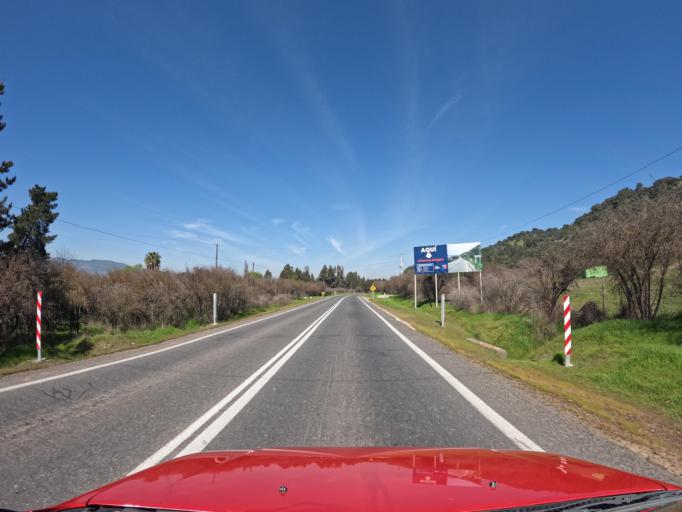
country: CL
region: Maule
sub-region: Provincia de Curico
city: Rauco
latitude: -34.9823
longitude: -71.4218
